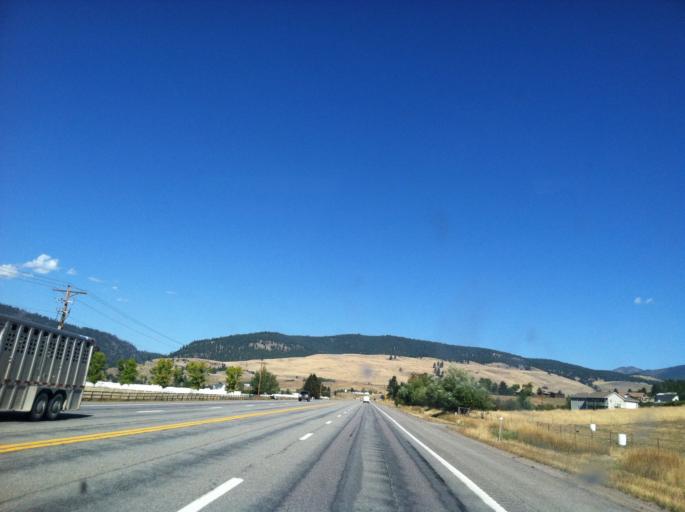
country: US
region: Montana
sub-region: Missoula County
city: Frenchtown
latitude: 46.9709
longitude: -114.1300
